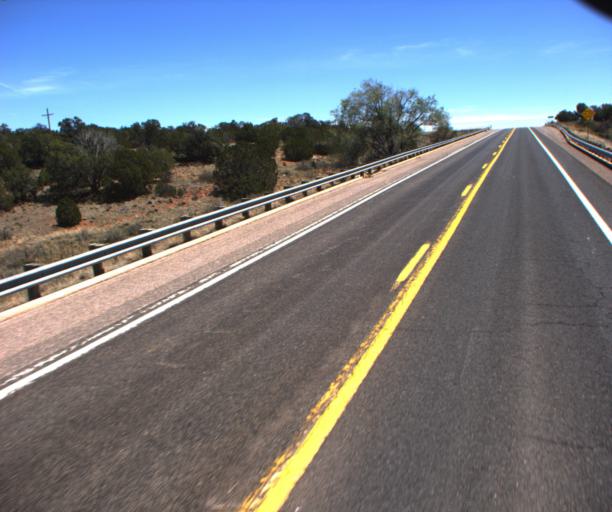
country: US
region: Arizona
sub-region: Mohave County
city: Peach Springs
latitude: 35.5216
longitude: -113.2078
